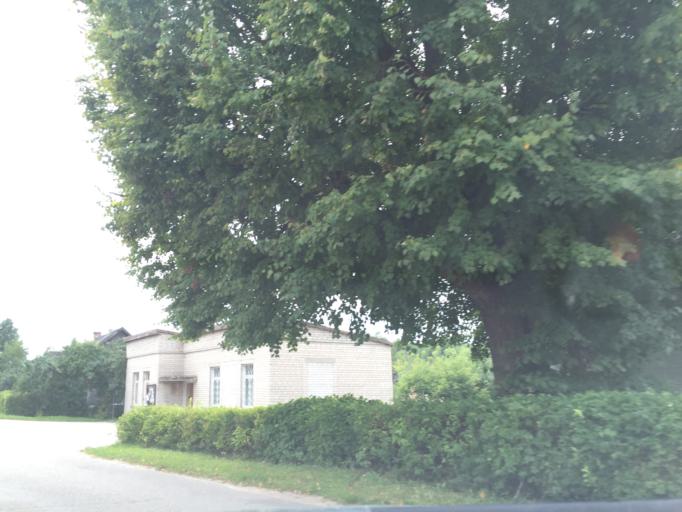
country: LV
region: Zilupes
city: Zilupe
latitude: 56.2640
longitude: 27.9879
